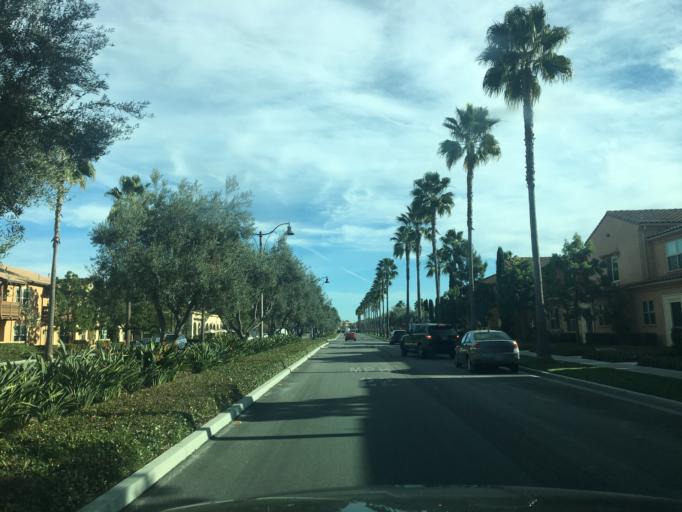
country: US
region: California
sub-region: Orange County
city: Laguna Woods
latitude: 33.6458
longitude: -117.7503
